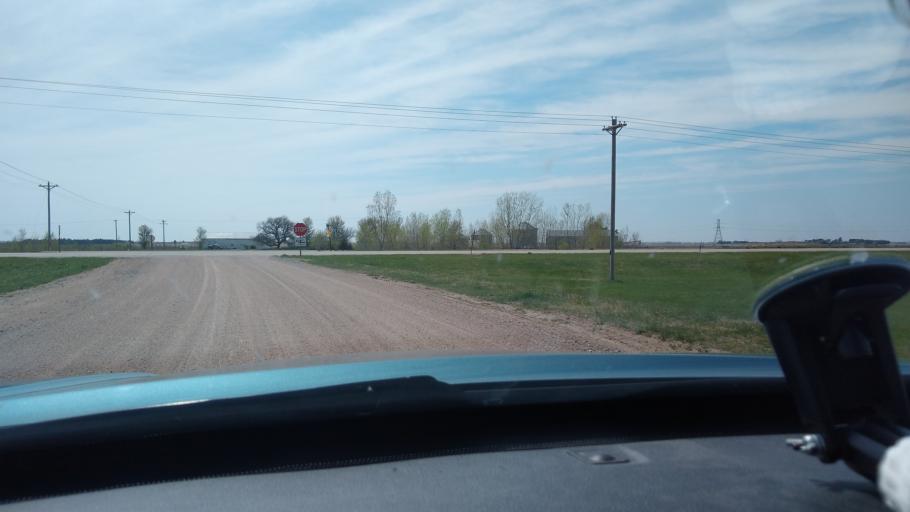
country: US
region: Nebraska
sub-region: Fillmore County
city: Geneva
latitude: 40.4154
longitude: -97.5933
